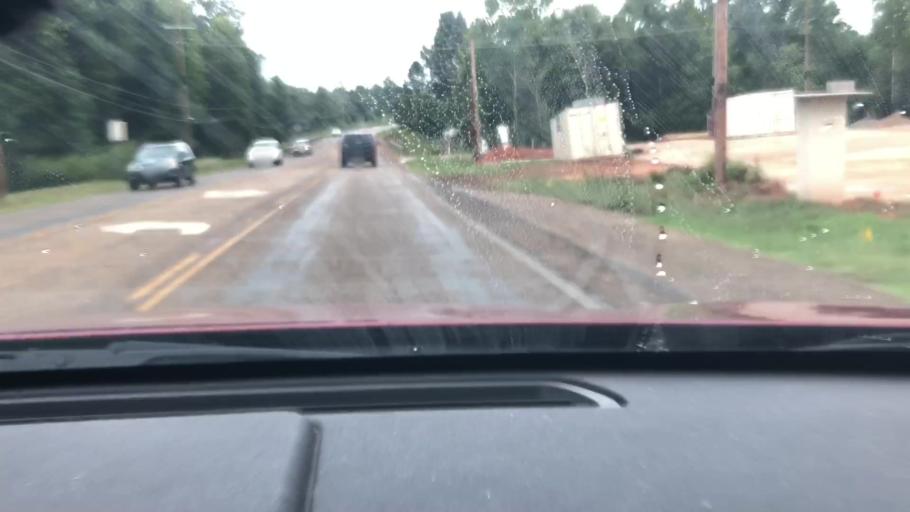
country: US
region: Texas
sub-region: Bowie County
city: Wake Village
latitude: 33.4432
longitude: -94.1096
